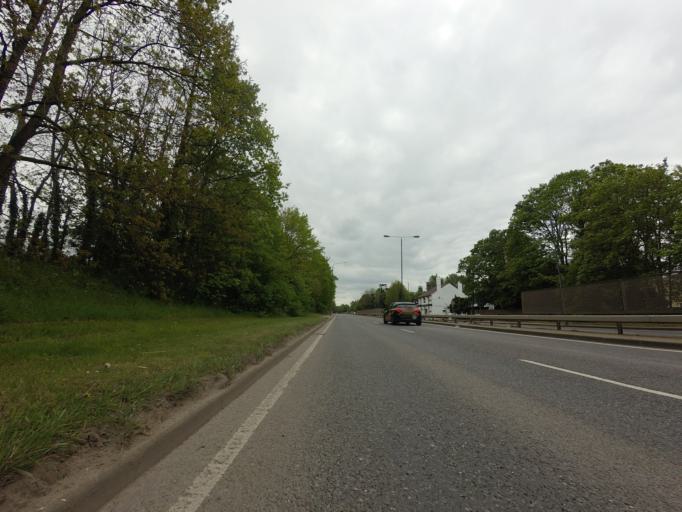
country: GB
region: England
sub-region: Greater London
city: Bexley
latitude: 51.4308
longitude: 0.1405
